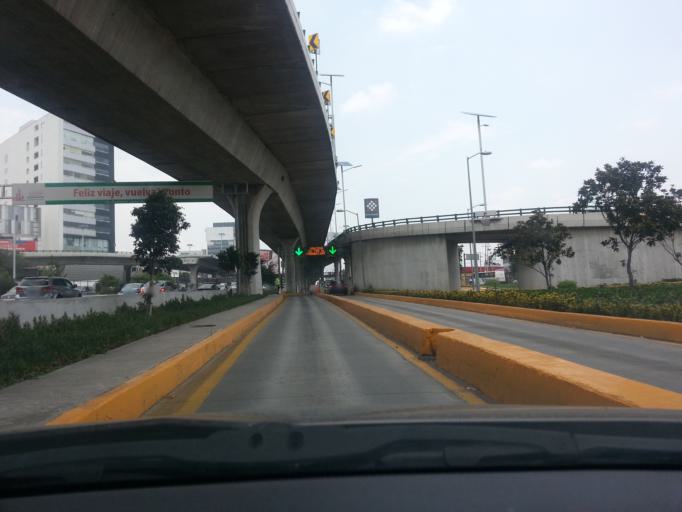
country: MX
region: Mexico
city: Vista Hermosa
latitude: 19.5174
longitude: -99.2316
